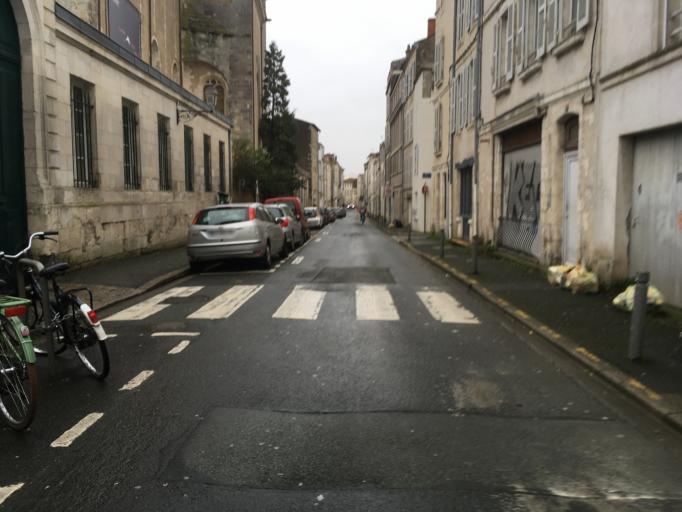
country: FR
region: Poitou-Charentes
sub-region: Departement de la Charente-Maritime
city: La Rochelle
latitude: 46.1635
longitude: -1.1509
